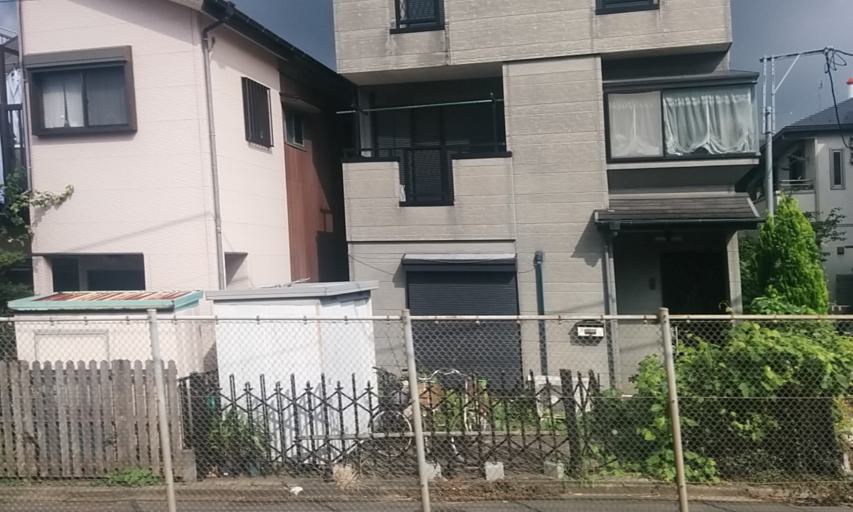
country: JP
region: Kanagawa
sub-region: Kawasaki-shi
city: Kawasaki
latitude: 35.5219
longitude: 139.6902
